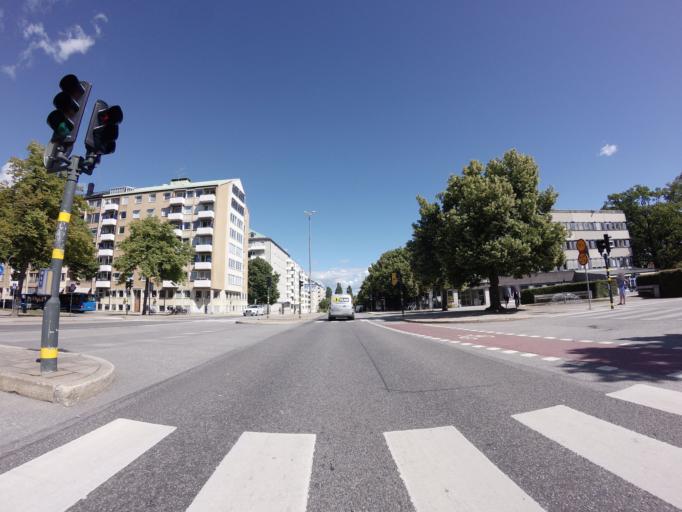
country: SE
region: Stockholm
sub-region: Stockholms Kommun
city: OEstermalm
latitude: 59.3353
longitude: 18.1008
